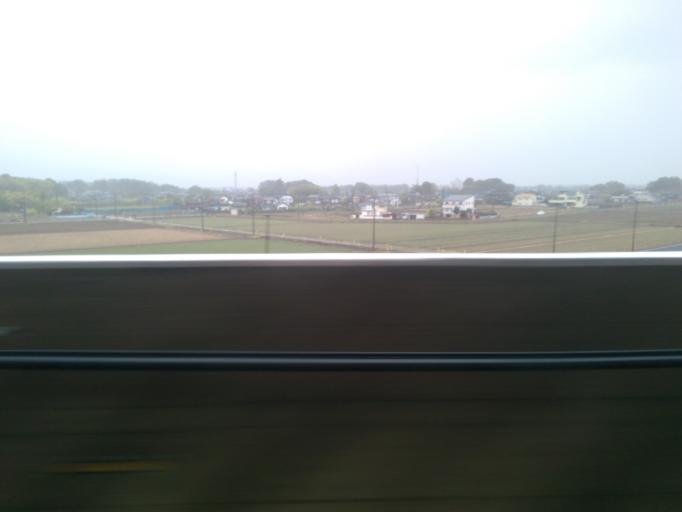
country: JP
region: Saitama
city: Shiraoka
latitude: 36.0116
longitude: 139.6479
